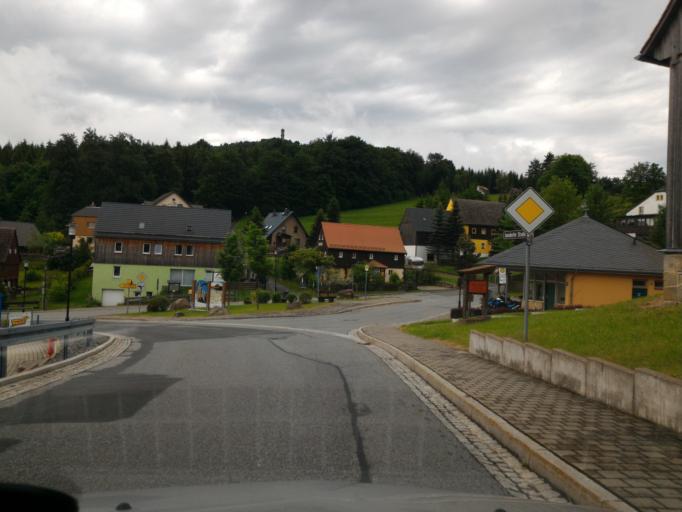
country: DE
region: Saxony
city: Kurort Oybin
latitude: 50.8338
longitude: 14.7219
